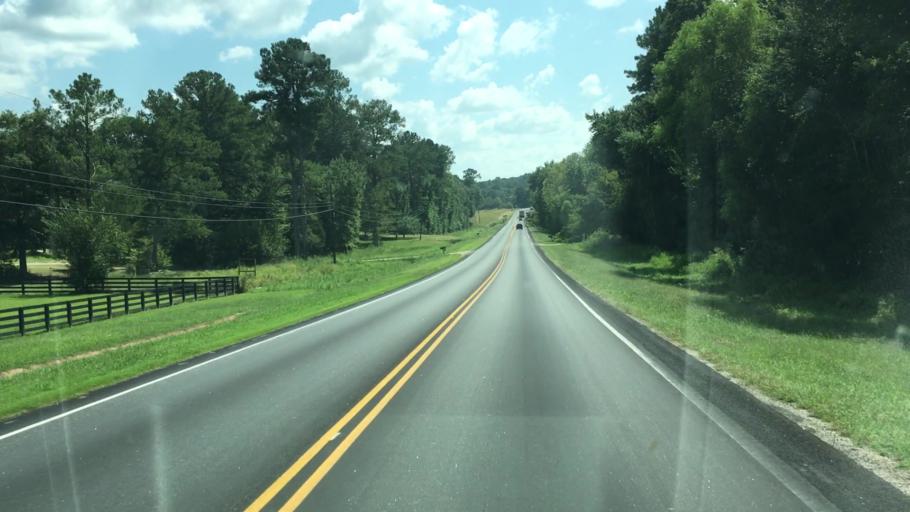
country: US
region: Georgia
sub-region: Morgan County
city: Madison
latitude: 33.6484
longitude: -83.4475
